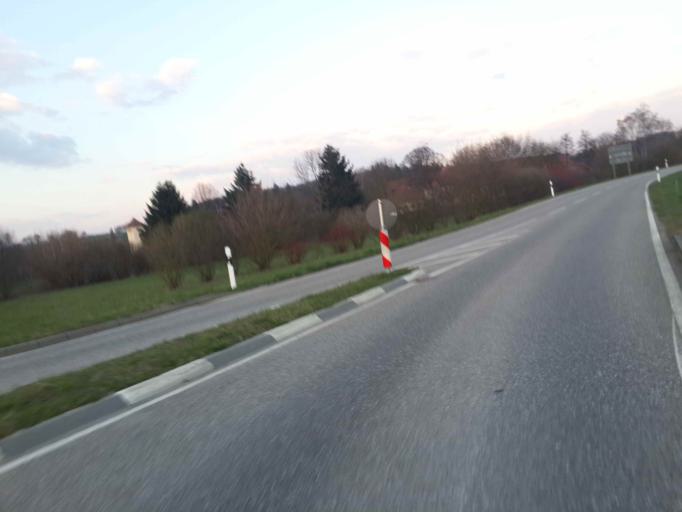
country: DE
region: Baden-Wuerttemberg
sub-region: Regierungsbezirk Stuttgart
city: Kirchardt
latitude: 49.2447
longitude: 9.0176
